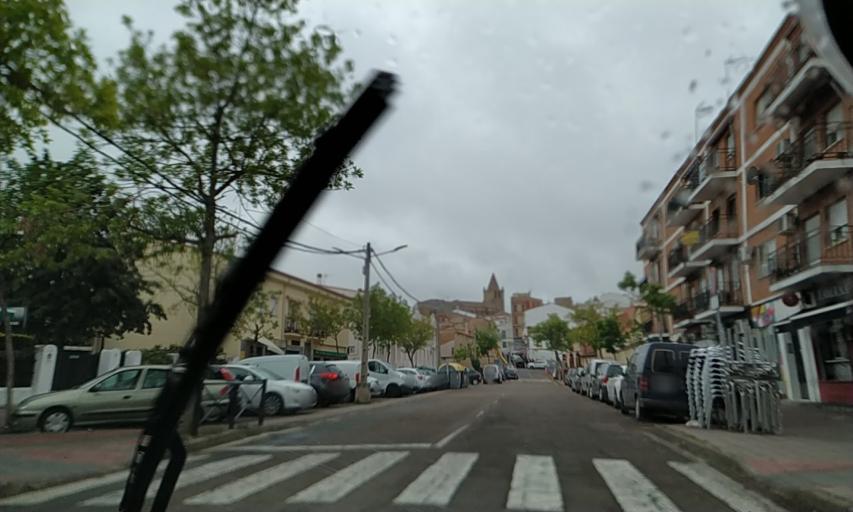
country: ES
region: Extremadura
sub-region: Provincia de Caceres
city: Caceres
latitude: 39.4794
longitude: -6.3694
